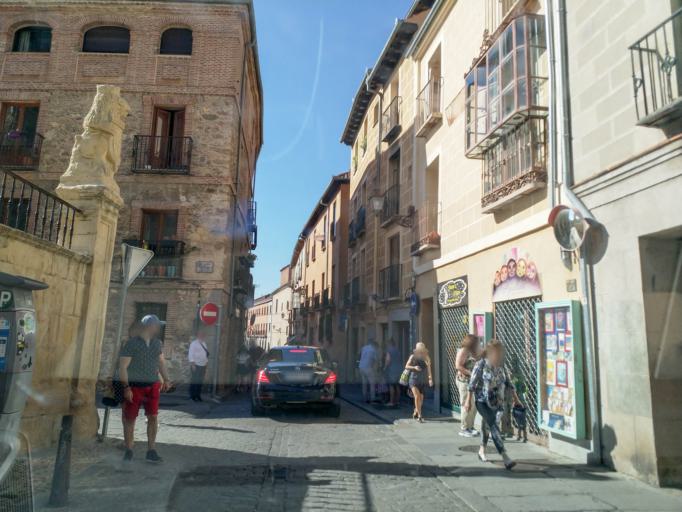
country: ES
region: Castille and Leon
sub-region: Provincia de Segovia
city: Segovia
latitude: 40.9509
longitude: -4.1258
